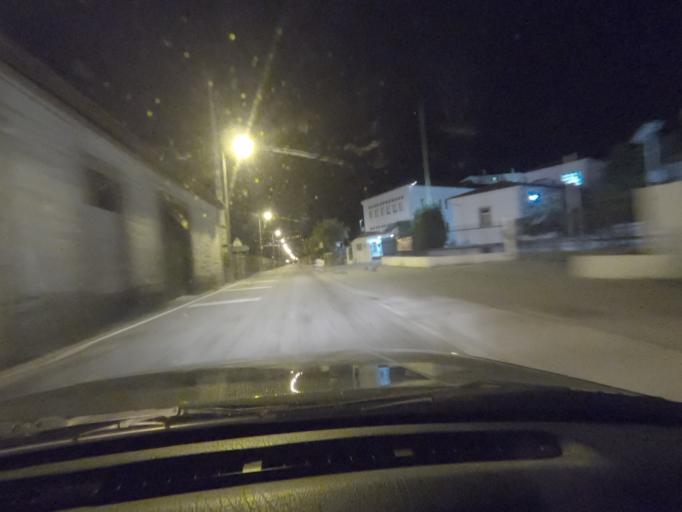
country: PT
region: Vila Real
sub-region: Peso da Regua
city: Godim
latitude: 41.1775
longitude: -7.7954
